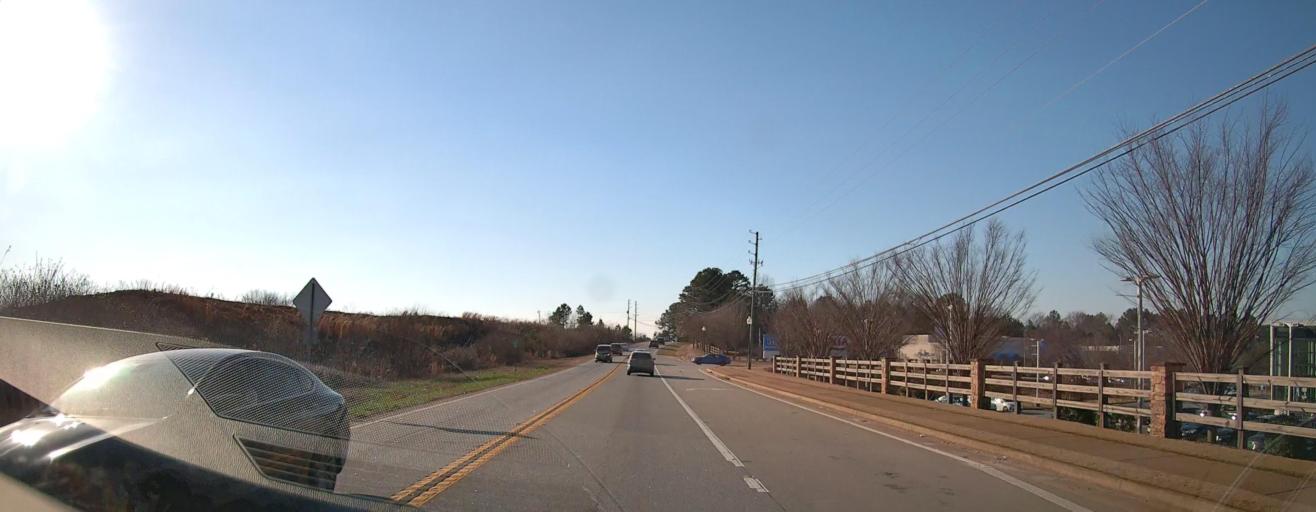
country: US
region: Georgia
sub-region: Henry County
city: McDonough
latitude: 33.4284
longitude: -84.1877
